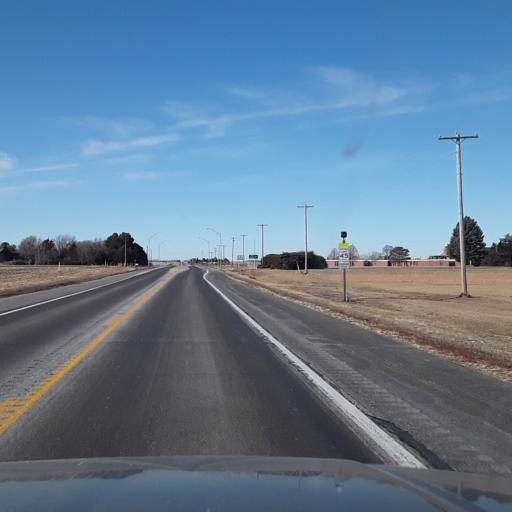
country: US
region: Nebraska
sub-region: Adams County
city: Hastings
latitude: 40.5681
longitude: -98.4554
